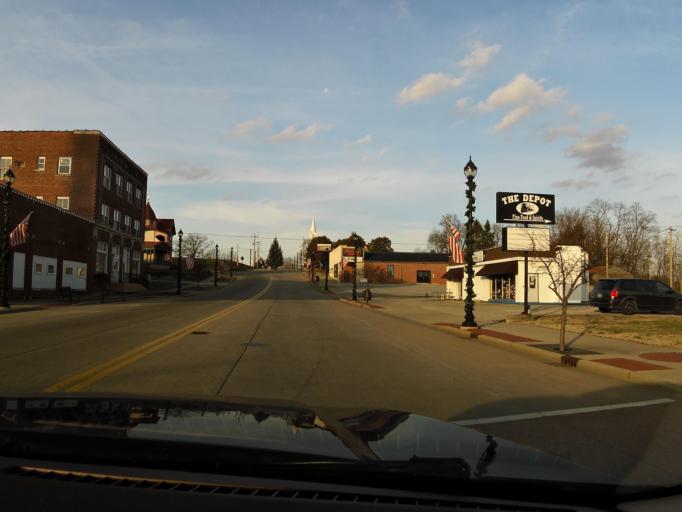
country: US
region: Illinois
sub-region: Fayette County
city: Vandalia
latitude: 38.9607
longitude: -89.0975
